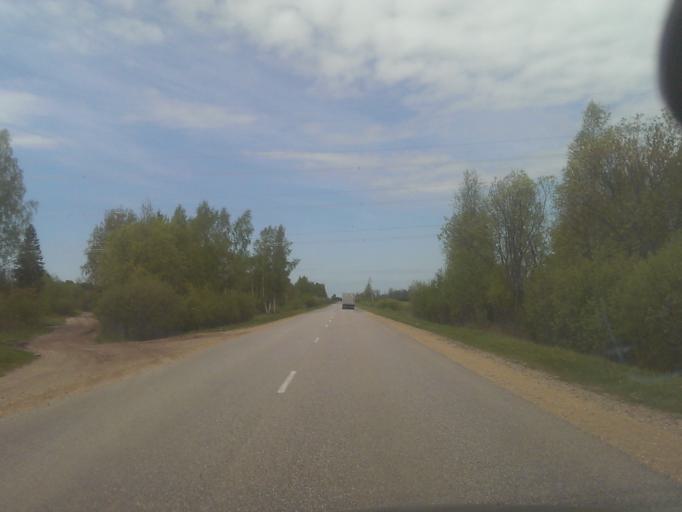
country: LV
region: Ventspils Rajons
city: Piltene
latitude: 57.1838
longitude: 21.6472
